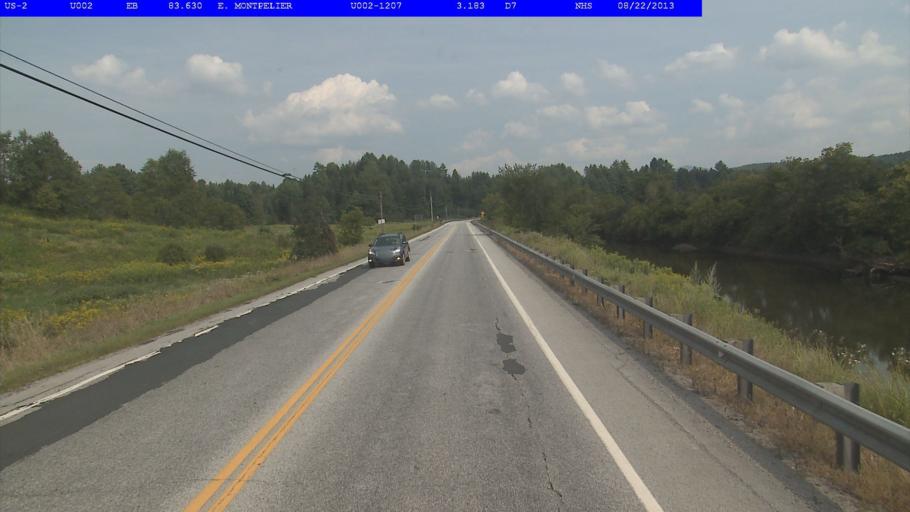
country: US
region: Vermont
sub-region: Washington County
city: Barre
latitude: 44.2718
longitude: -72.4820
